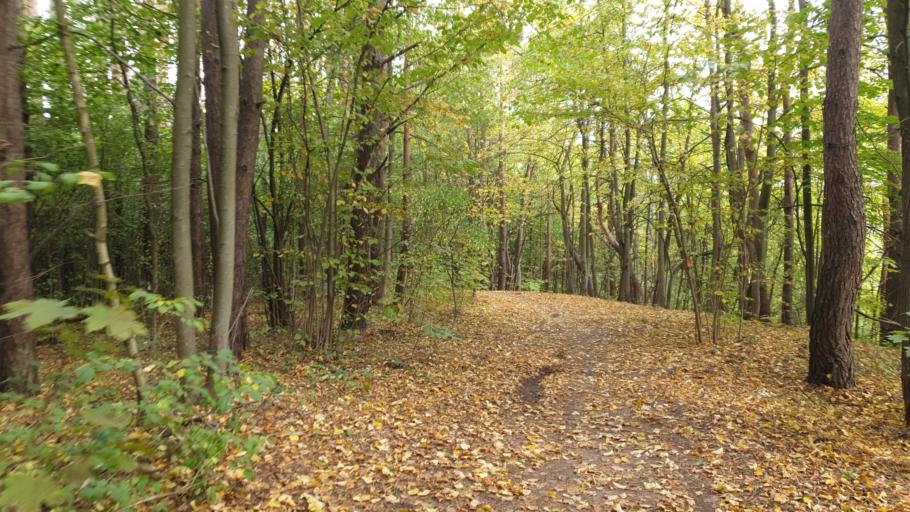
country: LT
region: Vilnius County
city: Seskine
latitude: 54.6928
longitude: 25.2340
